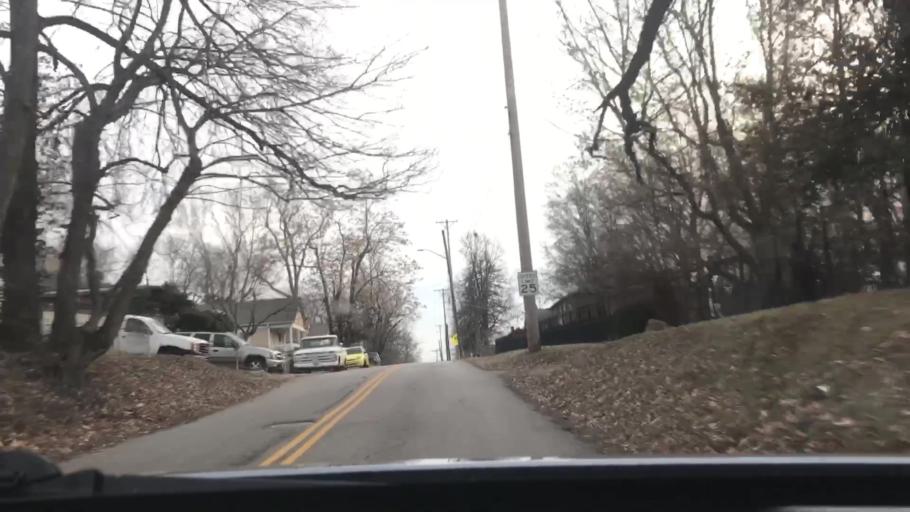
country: US
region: Missouri
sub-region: Jackson County
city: Independence
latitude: 39.0862
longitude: -94.4389
